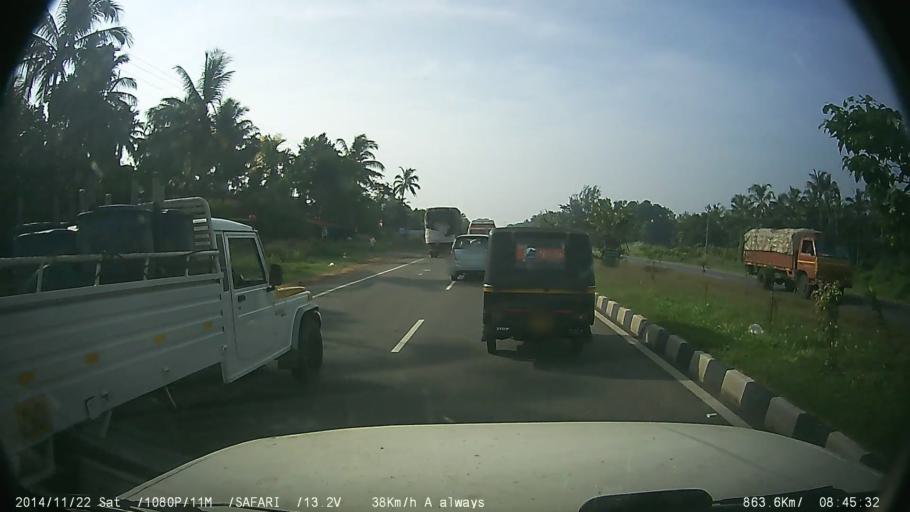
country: IN
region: Kerala
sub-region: Thrissur District
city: Trichur
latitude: 10.5049
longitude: 76.2583
